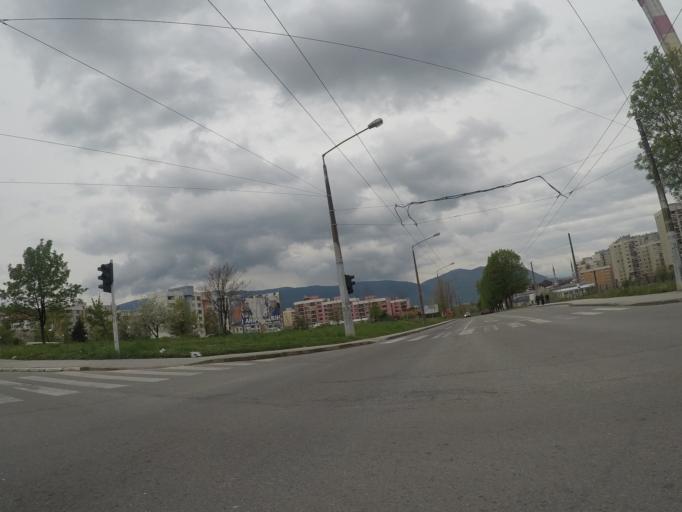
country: BA
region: Federation of Bosnia and Herzegovina
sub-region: Kanton Sarajevo
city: Sarajevo
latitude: 43.8401
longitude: 18.3490
